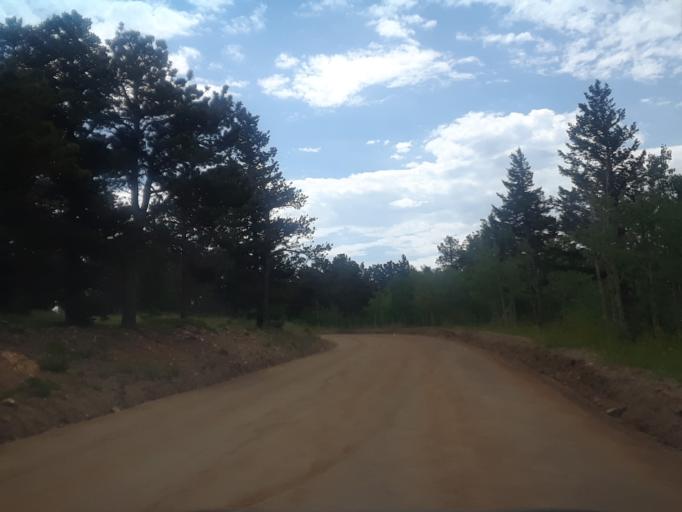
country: US
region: Colorado
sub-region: Boulder County
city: Nederland
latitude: 40.0597
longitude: -105.4319
